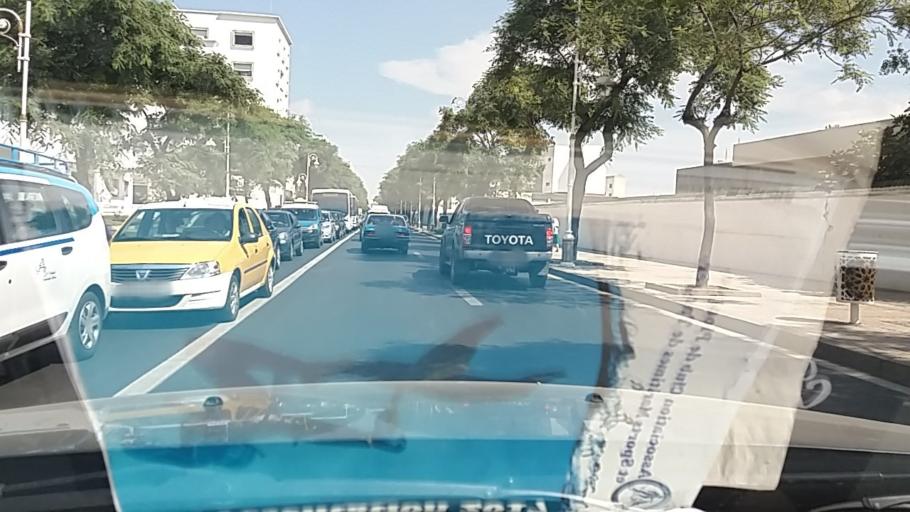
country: MA
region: Tanger-Tetouan
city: Tetouan
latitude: 35.5670
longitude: -5.3661
